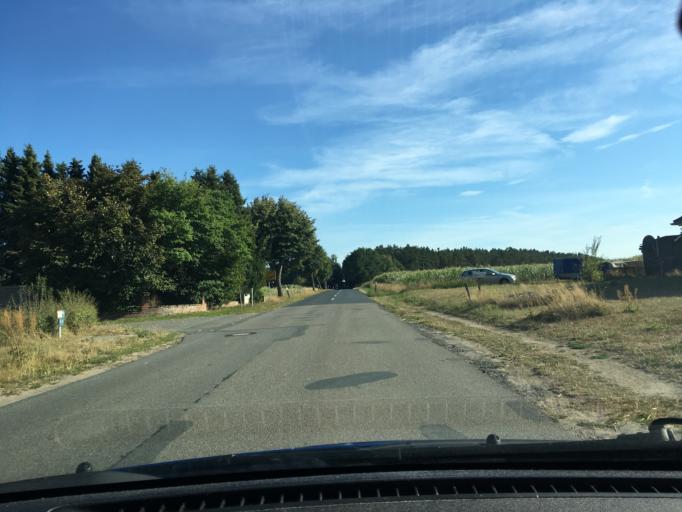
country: DE
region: Lower Saxony
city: Thomasburg
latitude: 53.2205
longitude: 10.7032
